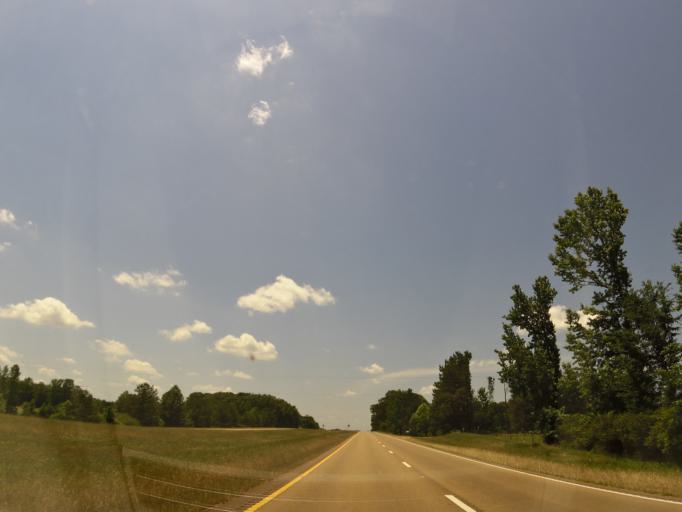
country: US
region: Mississippi
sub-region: Pontotoc County
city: Pontotoc
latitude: 34.3013
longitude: -89.2550
